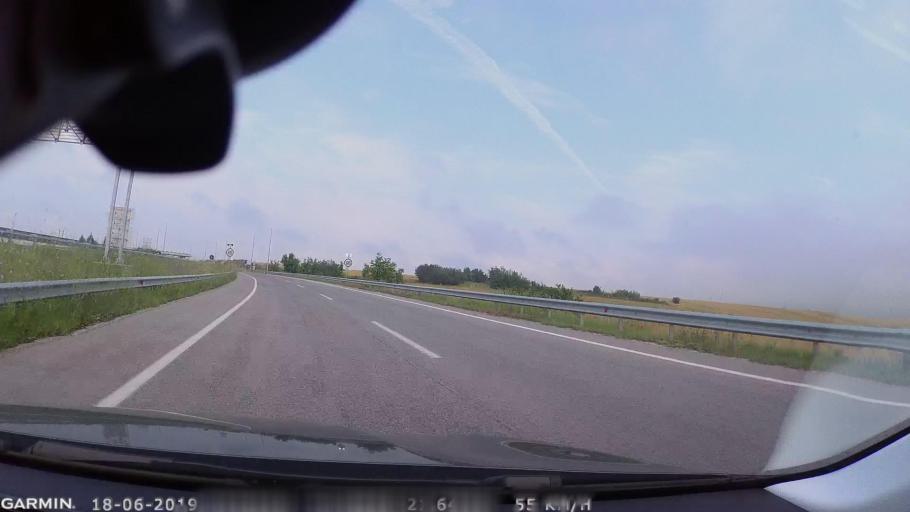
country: MK
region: Petrovec
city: Sredno Konjare
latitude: 41.9544
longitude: 21.7510
